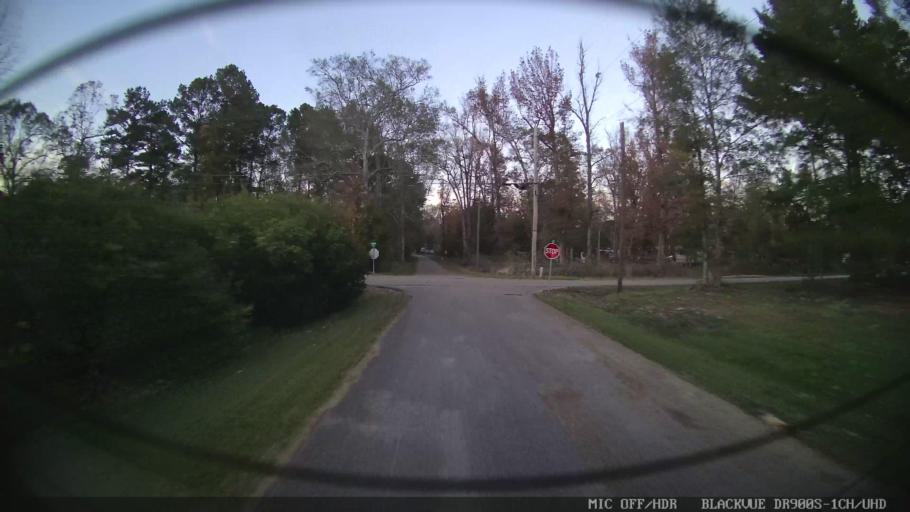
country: US
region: Mississippi
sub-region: Stone County
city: Wiggins
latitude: 31.0571
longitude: -89.1915
